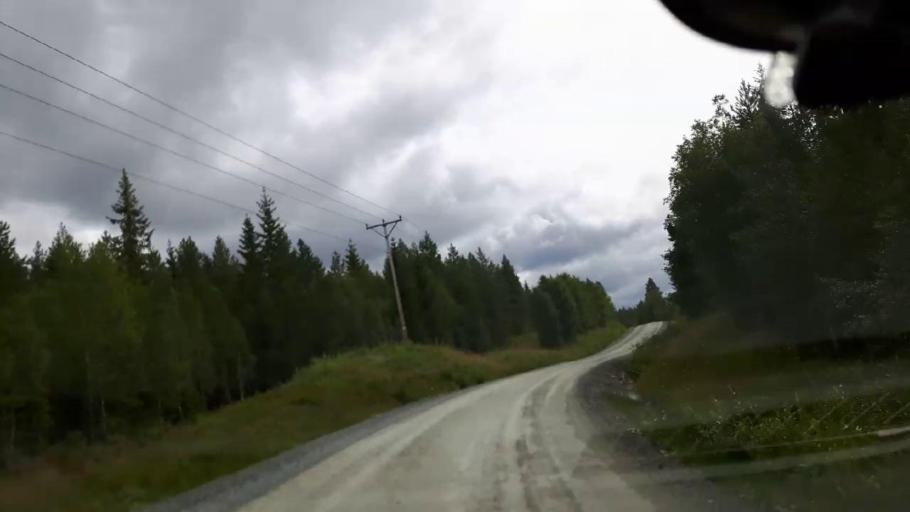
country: SE
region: Jaemtland
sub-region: Krokoms Kommun
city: Valla
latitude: 63.6039
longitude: 14.1320
